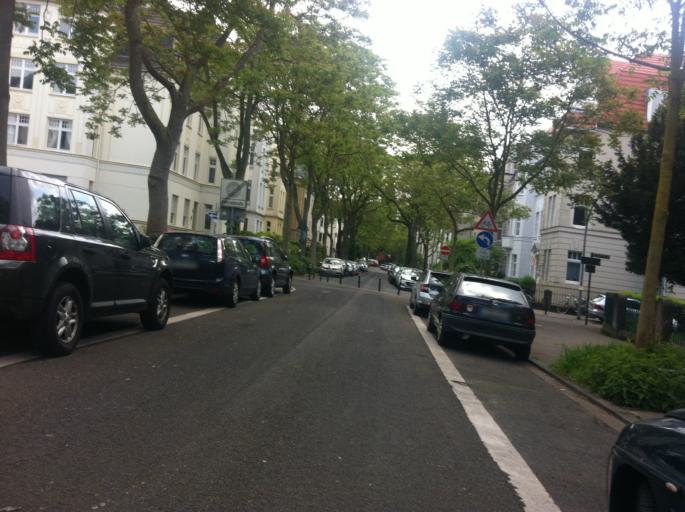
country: DE
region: North Rhine-Westphalia
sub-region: Regierungsbezirk Koln
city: Neuehrenfeld
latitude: 50.9569
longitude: 6.9209
